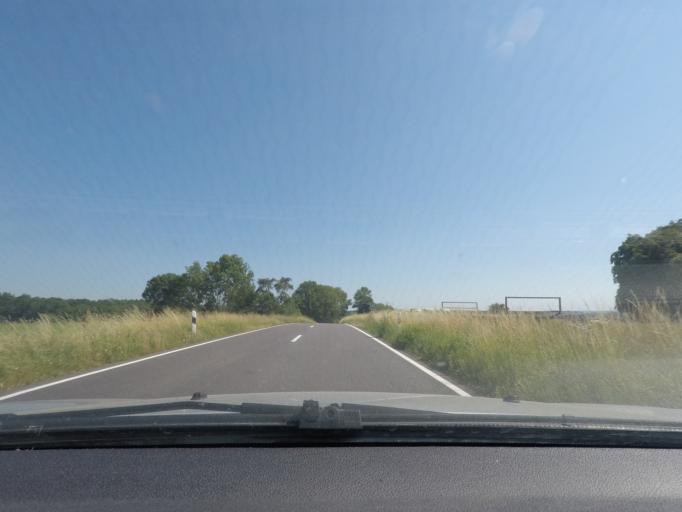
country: LU
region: Diekirch
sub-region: Canton de Redange
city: Ell
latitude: 49.7368
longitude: 5.8459
